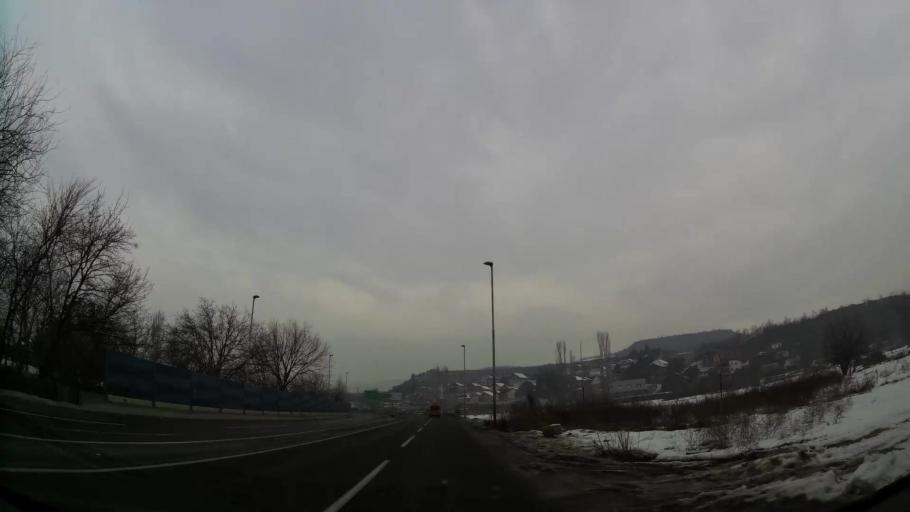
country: MK
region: Saraj
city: Saraj
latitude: 42.0077
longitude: 21.3293
